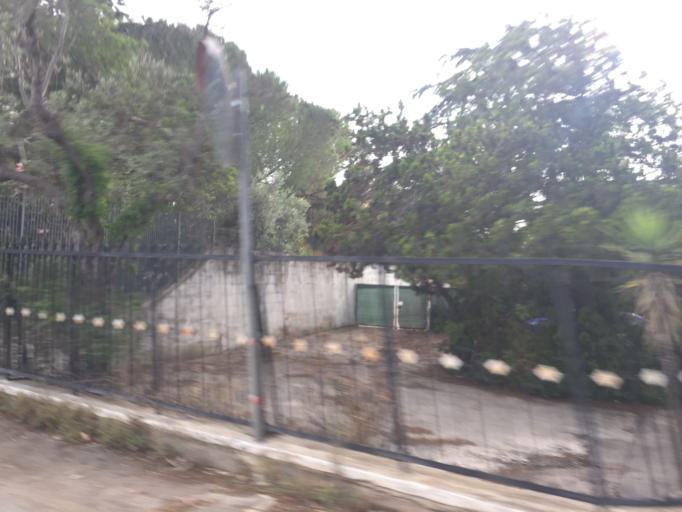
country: IT
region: Apulia
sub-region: Provincia di Bari
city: Capurso
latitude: 41.0552
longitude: 16.9216
